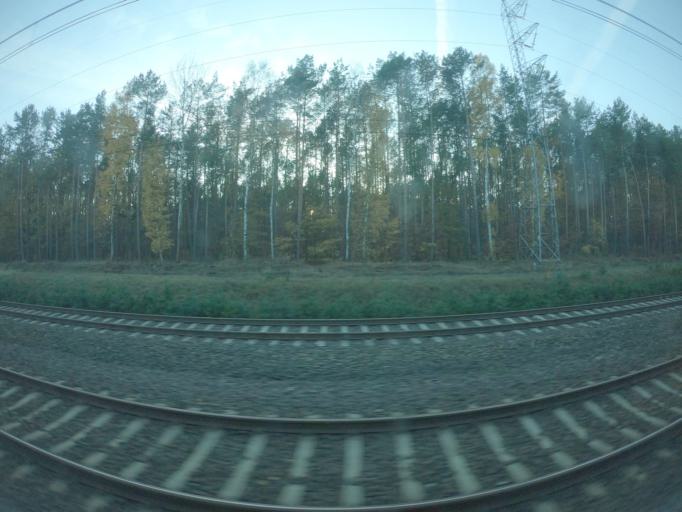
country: PL
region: Lubusz
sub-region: Powiat slubicki
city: Rzepin
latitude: 52.3143
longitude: 14.8582
